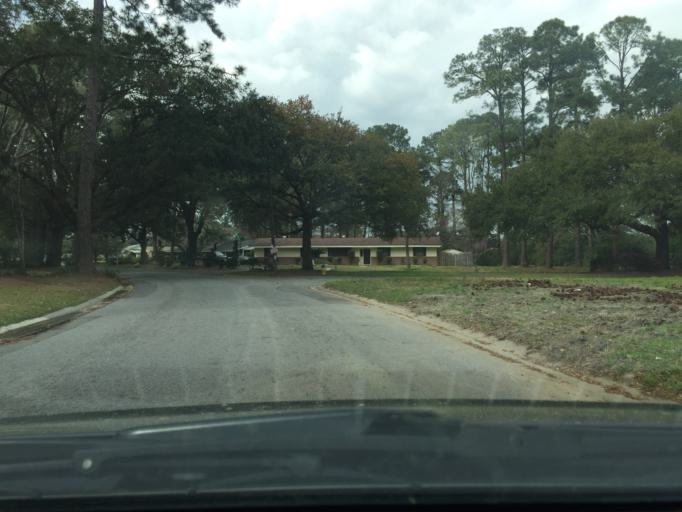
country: US
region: Georgia
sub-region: Chatham County
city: Montgomery
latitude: 31.9932
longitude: -81.1245
